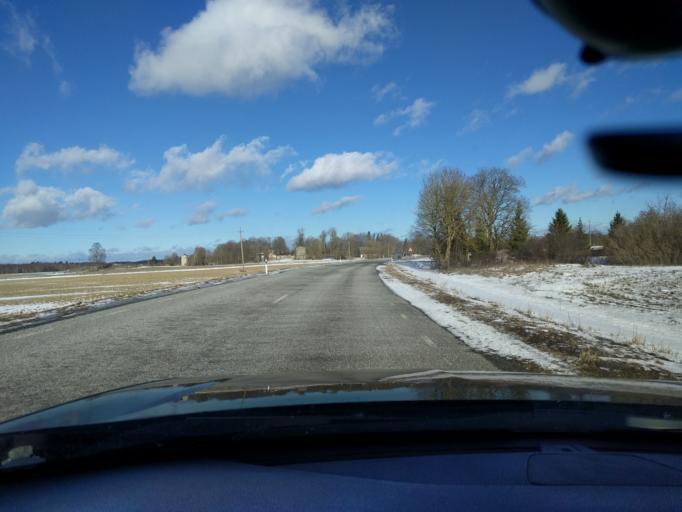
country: EE
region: Harju
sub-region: Raasiku vald
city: Raasiku
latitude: 59.3940
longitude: 25.1866
